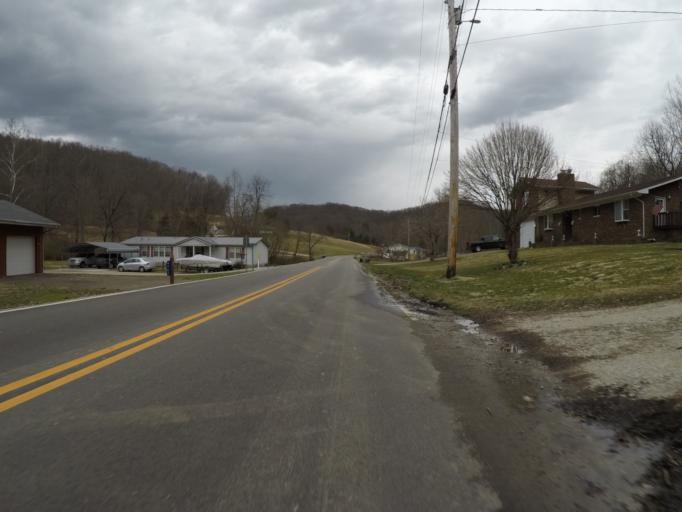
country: US
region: Ohio
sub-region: Lawrence County
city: Burlington
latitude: 38.4585
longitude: -82.5326
